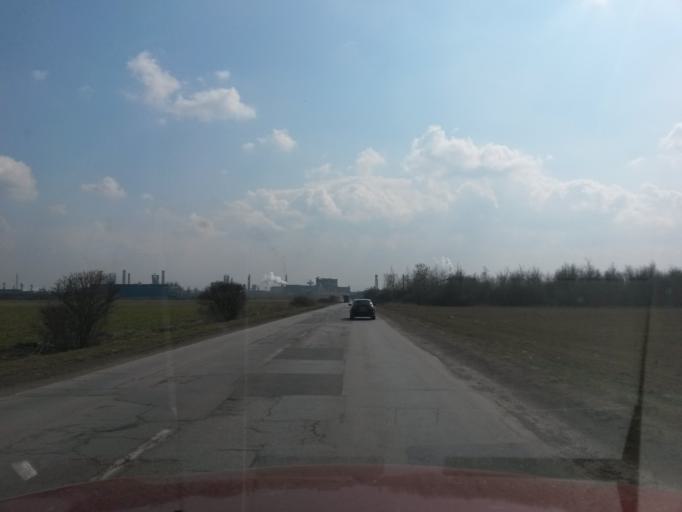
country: SK
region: Kosicky
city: Kosice
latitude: 48.6238
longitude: 21.1745
